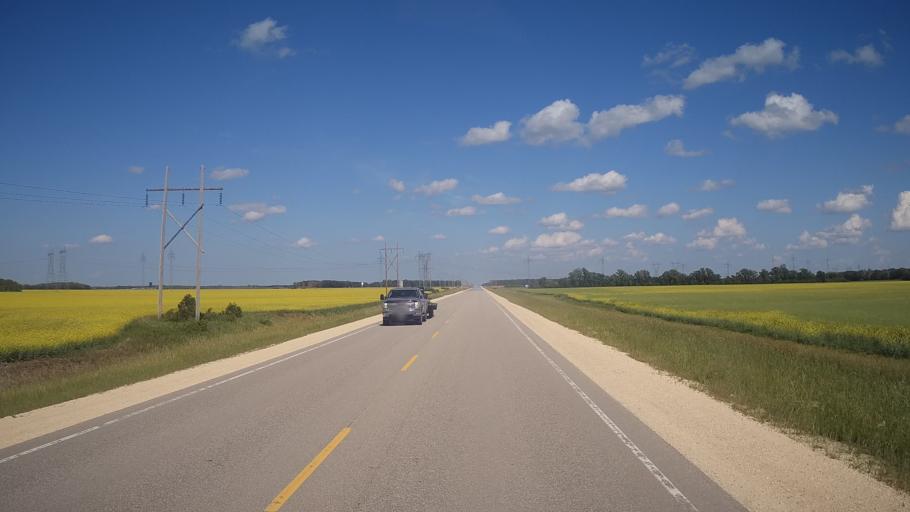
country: CA
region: Manitoba
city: Stonewall
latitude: 50.1227
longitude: -97.5015
